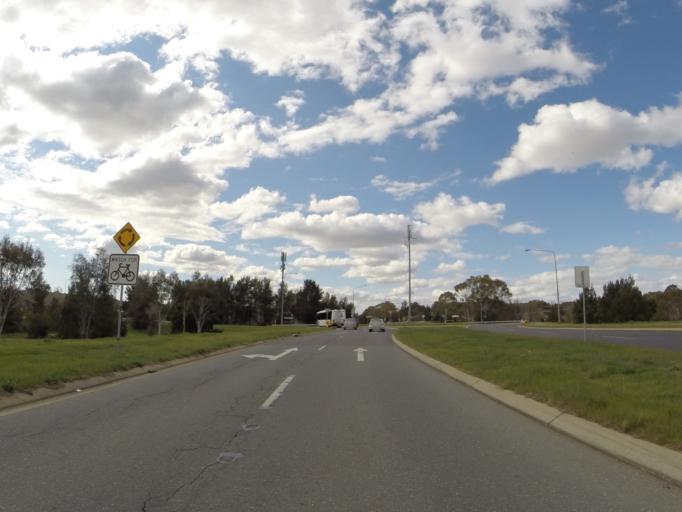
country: AU
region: Australian Capital Territory
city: Belconnen
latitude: -35.2142
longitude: 149.0864
